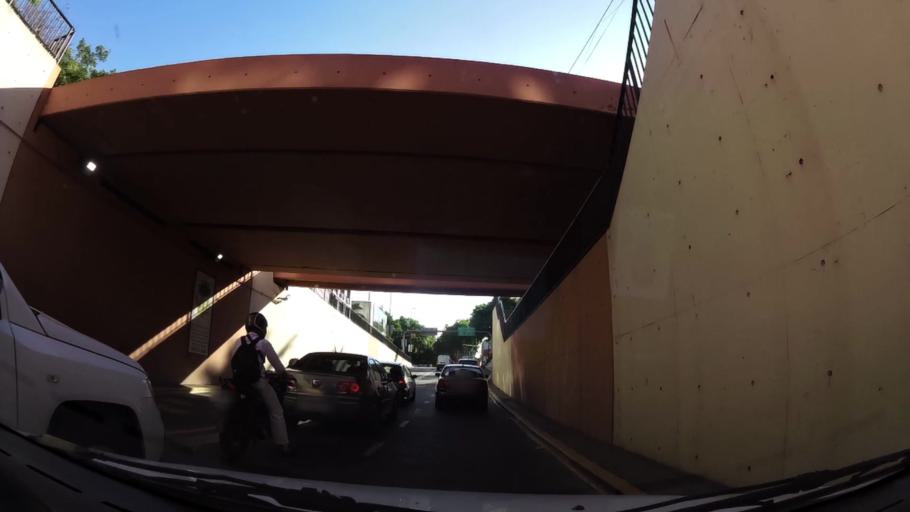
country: AR
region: Buenos Aires
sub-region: Partido de San Isidro
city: San Isidro
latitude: -34.4738
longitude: -58.5117
